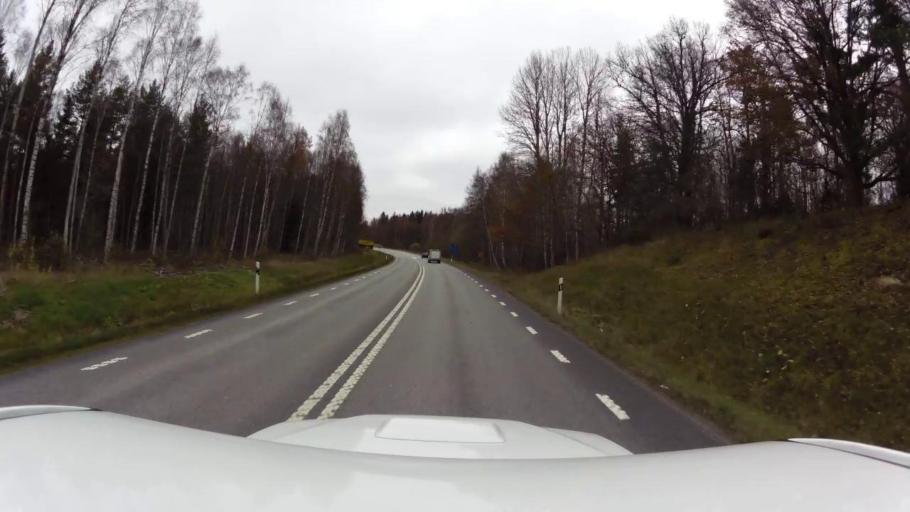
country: SE
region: OEstergoetland
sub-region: Kinda Kommun
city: Rimforsa
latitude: 58.1605
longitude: 15.6813
